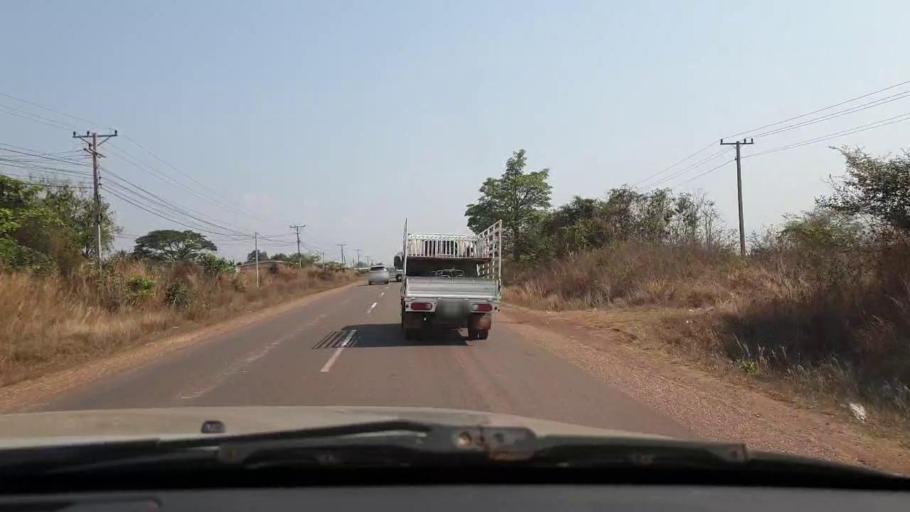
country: TH
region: Nong Khai
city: Phon Phisai
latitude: 18.0691
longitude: 102.9062
